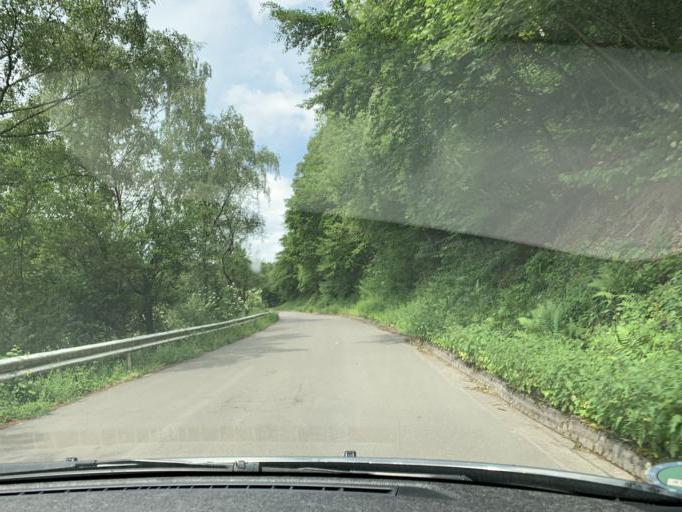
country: DE
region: North Rhine-Westphalia
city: Heimbach
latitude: 50.6521
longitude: 6.4098
